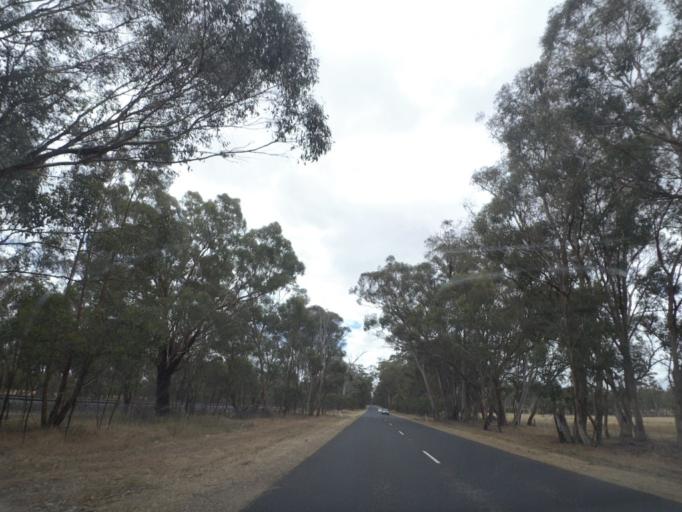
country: AU
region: Victoria
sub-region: Murrindindi
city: Kinglake West
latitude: -36.9771
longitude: 145.1626
